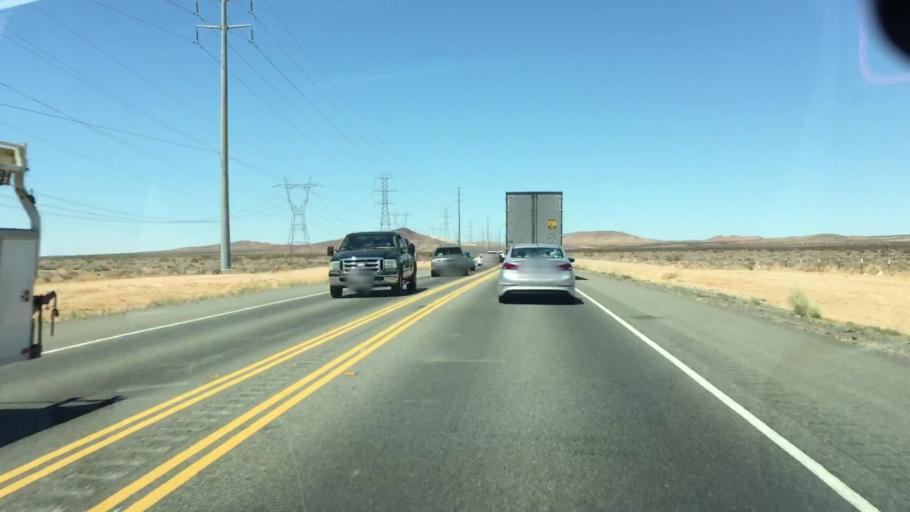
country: US
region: California
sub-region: Kern County
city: Boron
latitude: 34.8371
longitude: -117.4985
